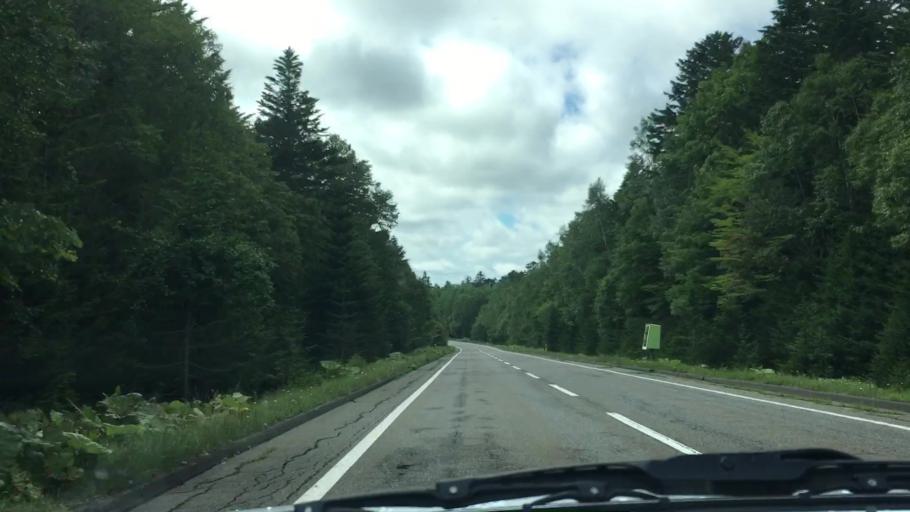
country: JP
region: Hokkaido
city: Kitami
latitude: 43.4177
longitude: 143.9765
